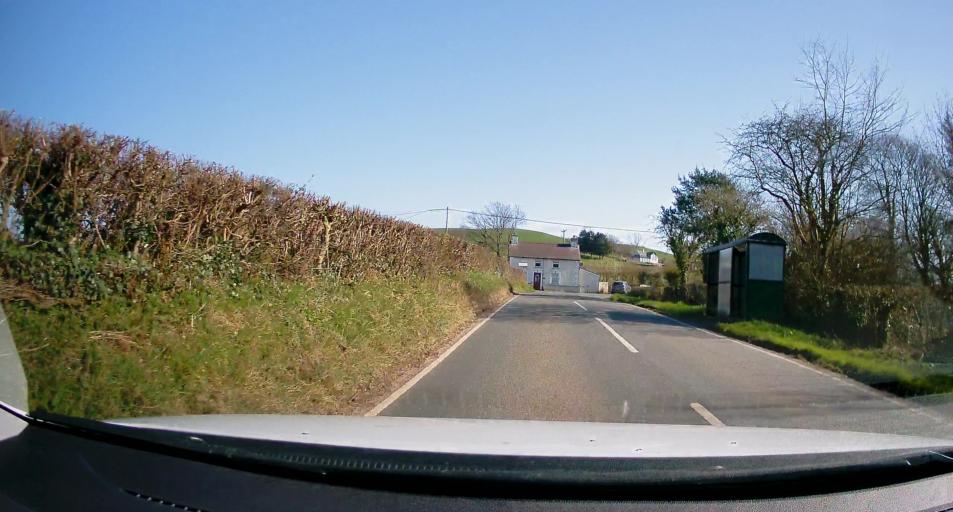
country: GB
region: Wales
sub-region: County of Ceredigion
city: Penparcau
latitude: 52.3542
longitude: -4.0556
